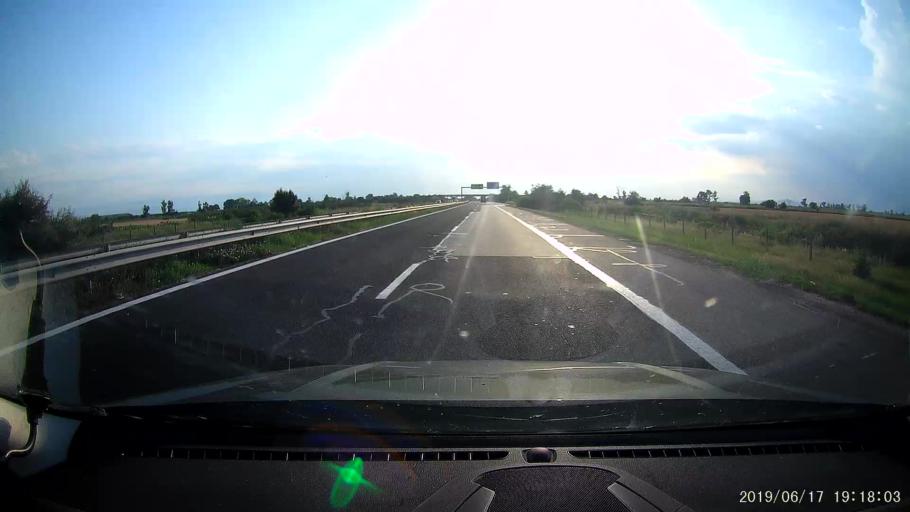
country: BG
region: Plovdiv
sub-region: Obshtina Suedinenie
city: Suedinenie
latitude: 42.2042
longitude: 24.5713
